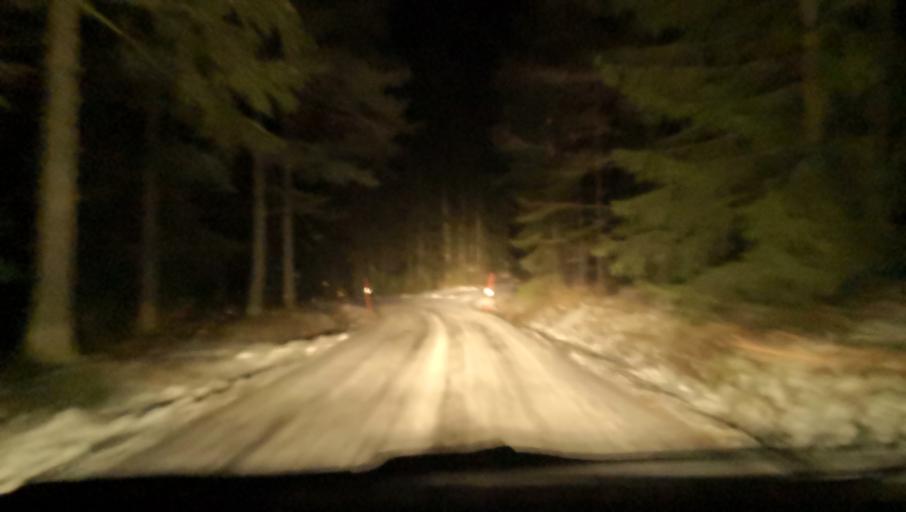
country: SE
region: Uppsala
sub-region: Enkopings Kommun
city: Hummelsta
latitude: 59.6326
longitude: 16.8766
